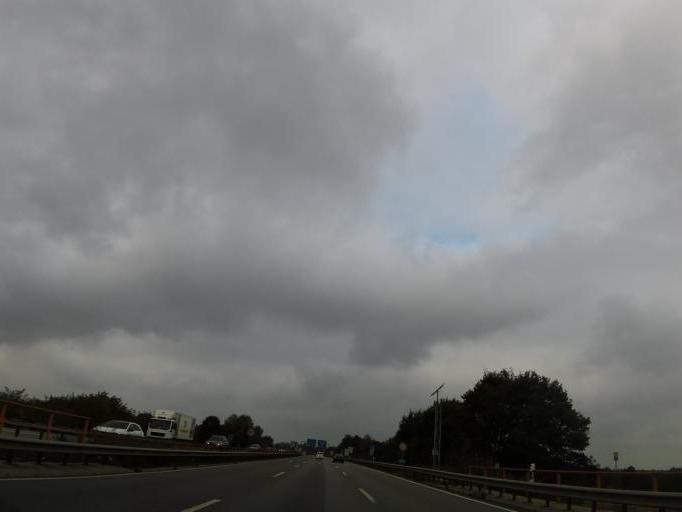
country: DE
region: Rheinland-Pfalz
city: Landstuhl
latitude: 49.4217
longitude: 7.5659
